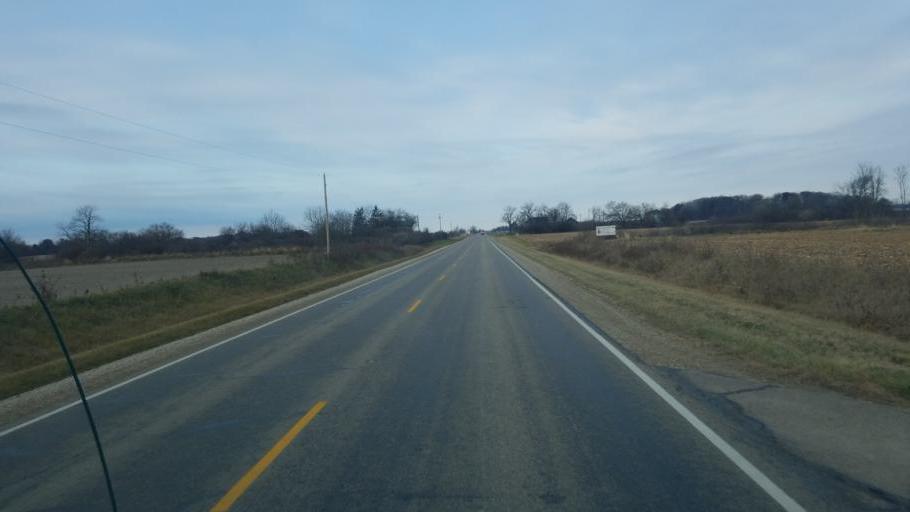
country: US
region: Indiana
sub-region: Adams County
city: Geneva
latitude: 40.5423
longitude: -84.8803
